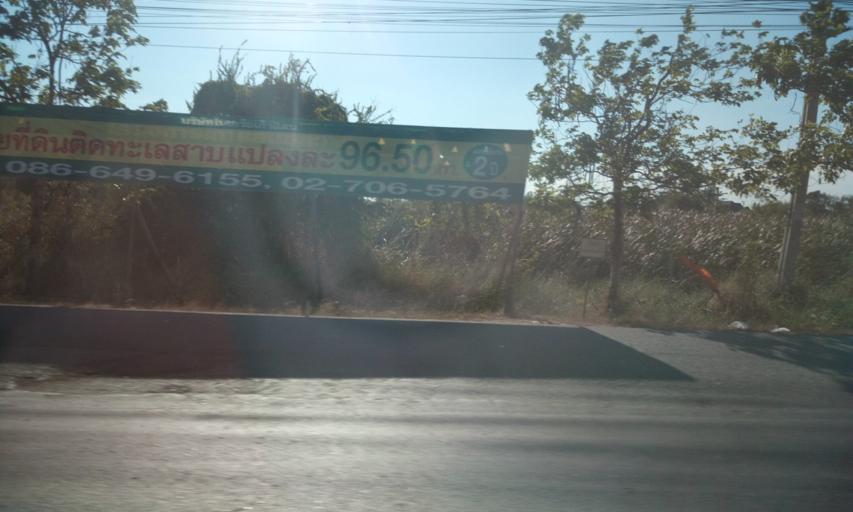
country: TH
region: Samut Prakan
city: Bang Bo District
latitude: 13.5876
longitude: 100.7596
